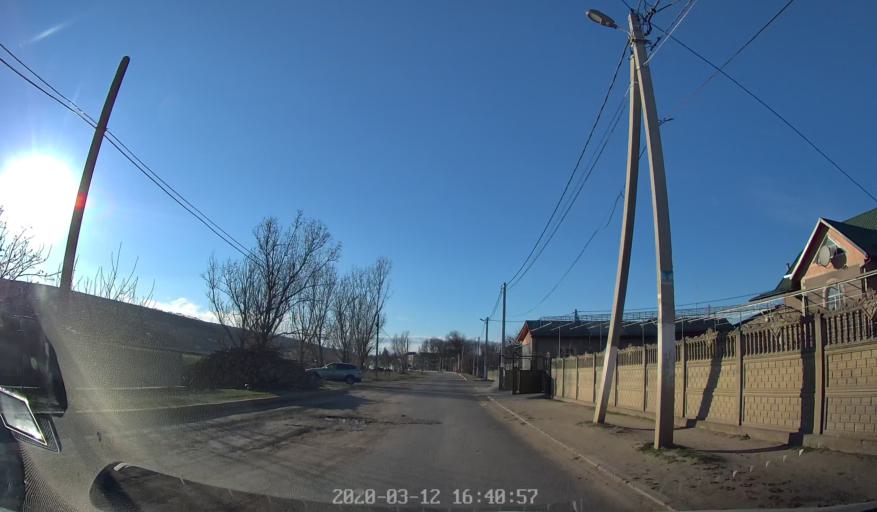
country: MD
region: Anenii Noi
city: Anenii Noi
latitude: 46.8198
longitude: 29.1421
